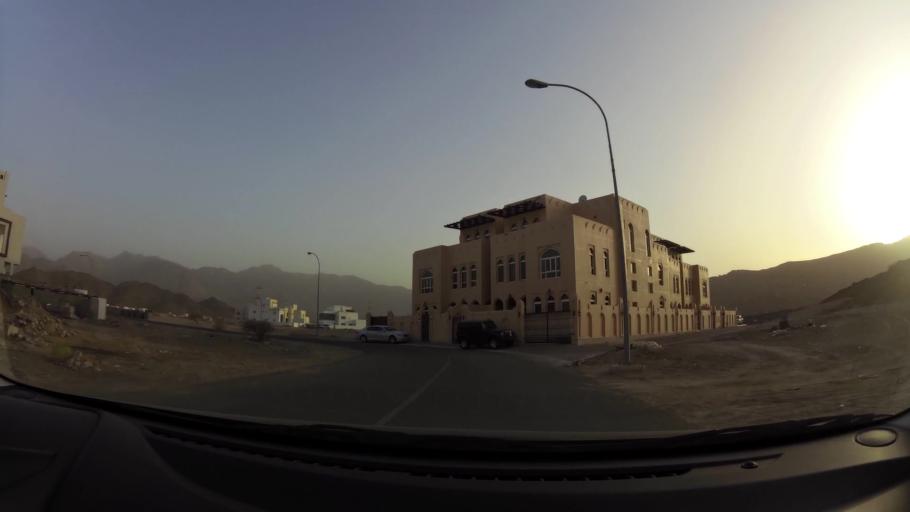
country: OM
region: Muhafazat Masqat
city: Bawshar
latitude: 23.4956
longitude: 58.3174
